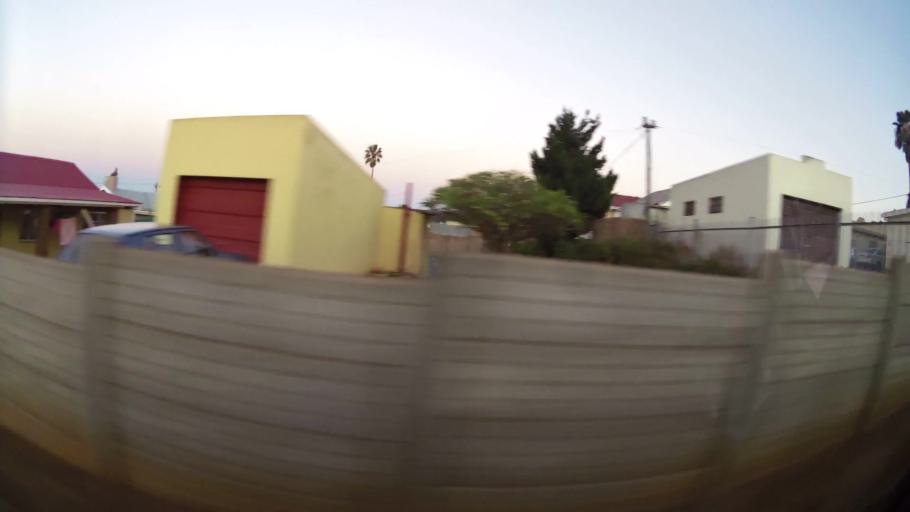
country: ZA
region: Western Cape
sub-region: Eden District Municipality
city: Riversdale
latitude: -34.0987
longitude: 21.2642
